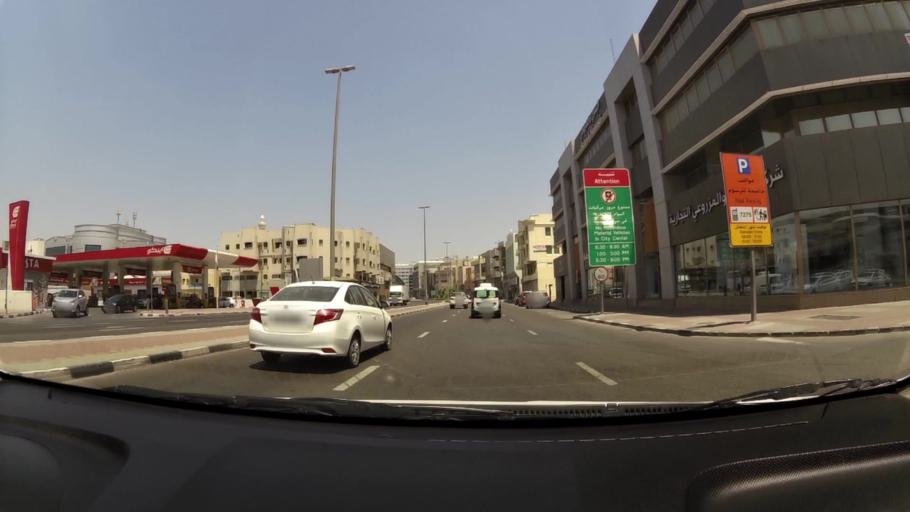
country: AE
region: Ash Shariqah
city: Sharjah
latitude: 25.2620
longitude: 55.3332
